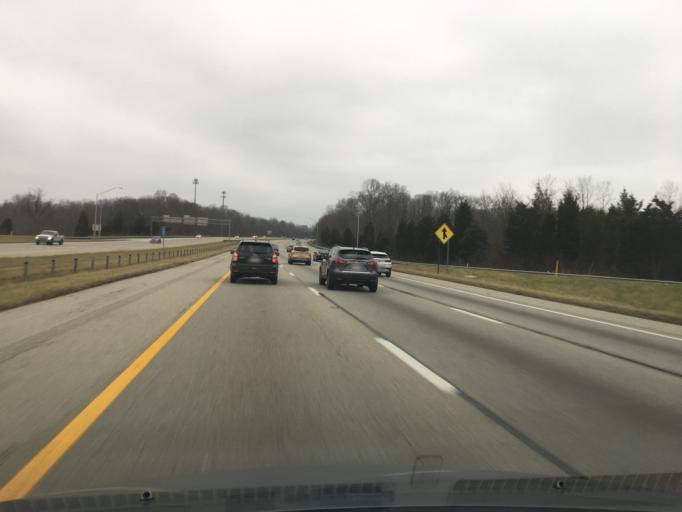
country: US
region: Ohio
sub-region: Hamilton County
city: The Village of Indian Hill
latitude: 39.2250
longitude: -84.2785
